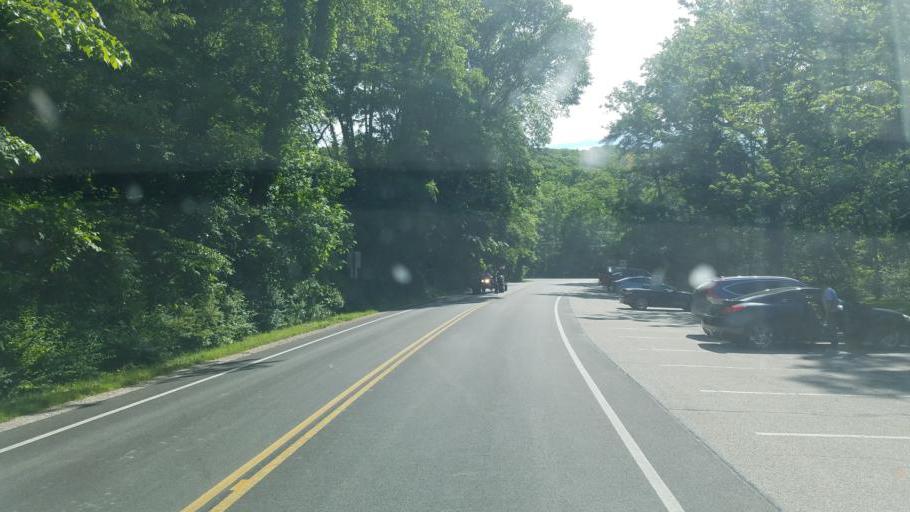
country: US
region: Ohio
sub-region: Summit County
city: Fairlawn
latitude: 41.1298
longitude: -81.5522
